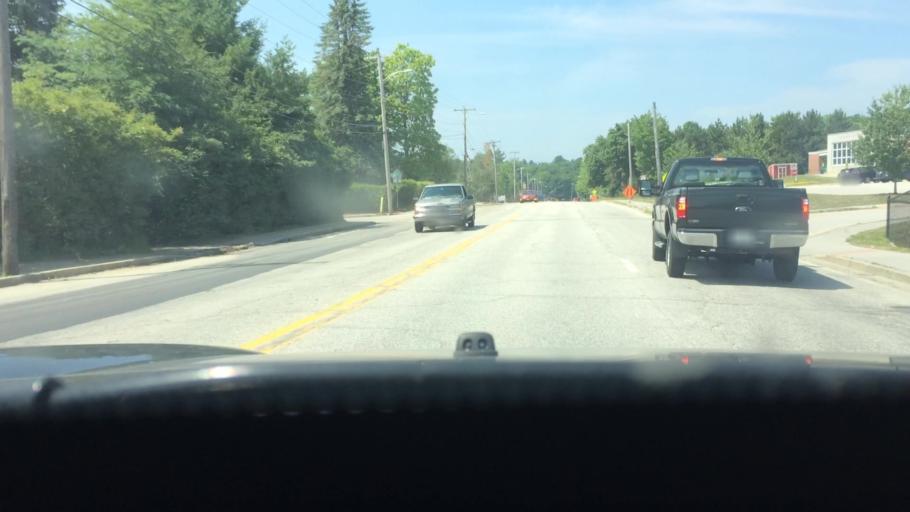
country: US
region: Maine
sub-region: Androscoggin County
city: Auburn
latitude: 44.0843
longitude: -70.2431
